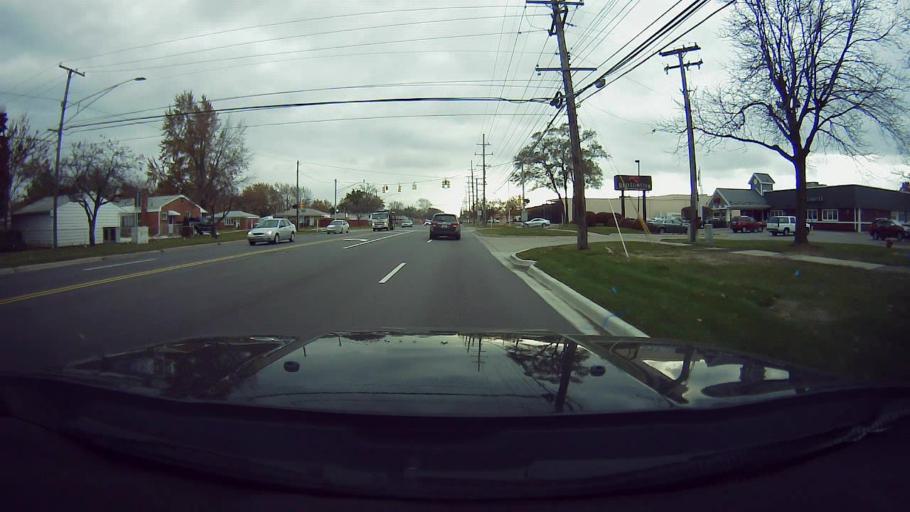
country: US
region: Michigan
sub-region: Macomb County
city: Center Line
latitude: 42.4852
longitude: -83.0064
